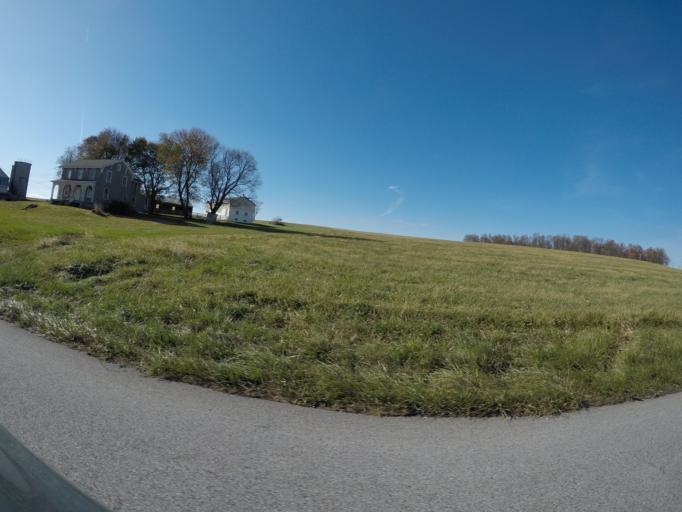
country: US
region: Pennsylvania
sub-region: Chester County
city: Parkesburg
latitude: 39.9350
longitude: -75.9107
